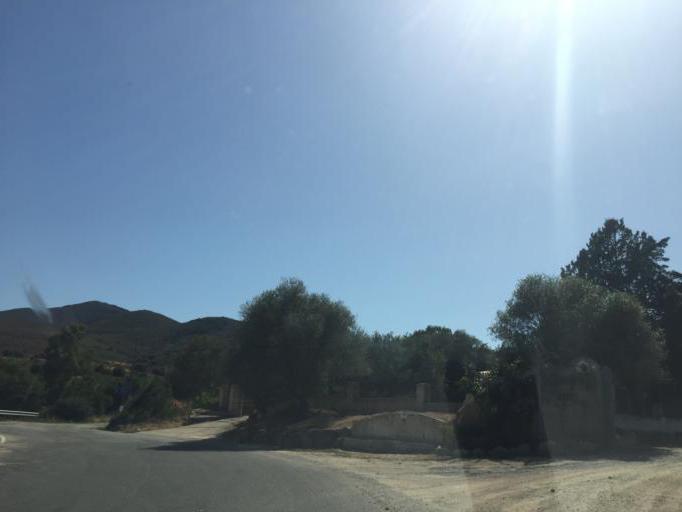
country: IT
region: Sardinia
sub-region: Provincia di Olbia-Tempio
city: San Teodoro
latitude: 40.7246
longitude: 9.6422
